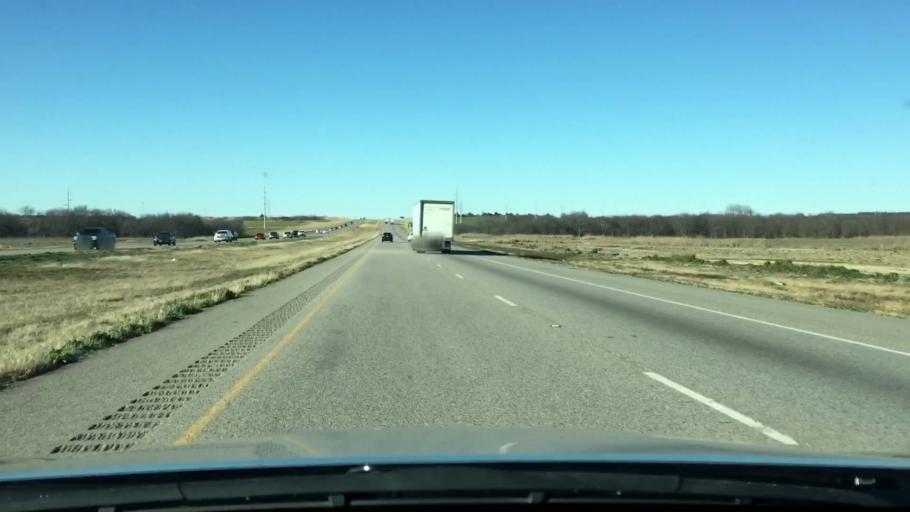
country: US
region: Texas
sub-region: Hill County
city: Itasca
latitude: 32.1317
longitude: -97.1196
